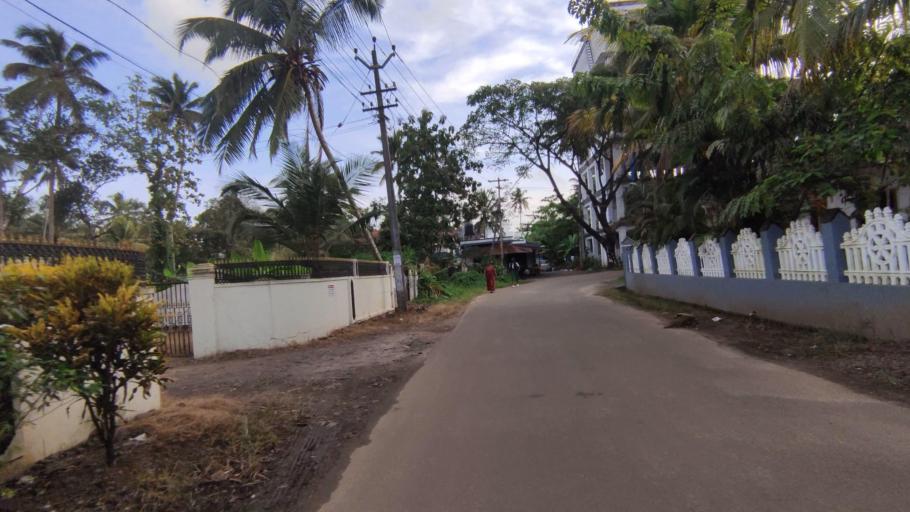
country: IN
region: Kerala
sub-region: Kottayam
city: Kottayam
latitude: 9.6037
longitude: 76.4345
